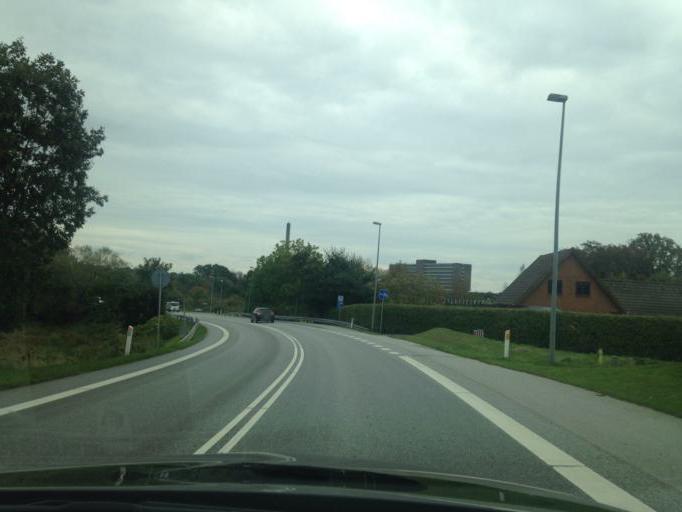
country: DK
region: South Denmark
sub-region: Haderslev Kommune
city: Haderslev
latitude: 55.2442
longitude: 9.4430
